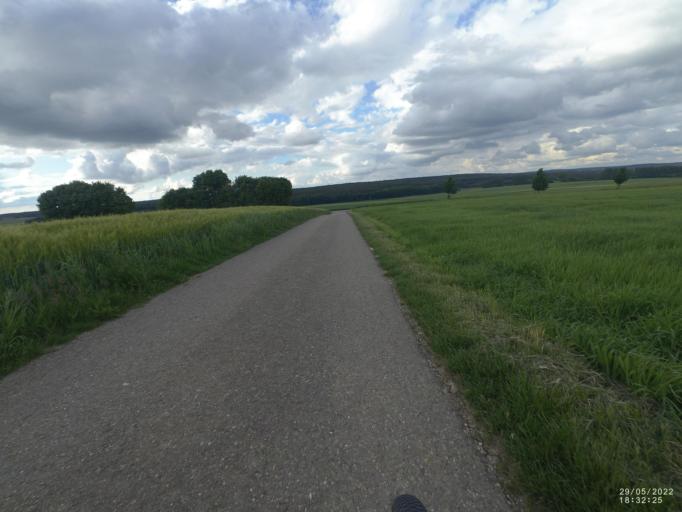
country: DE
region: Baden-Wuerttemberg
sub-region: Tuebingen Region
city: Ballendorf
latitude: 48.6017
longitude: 10.0964
